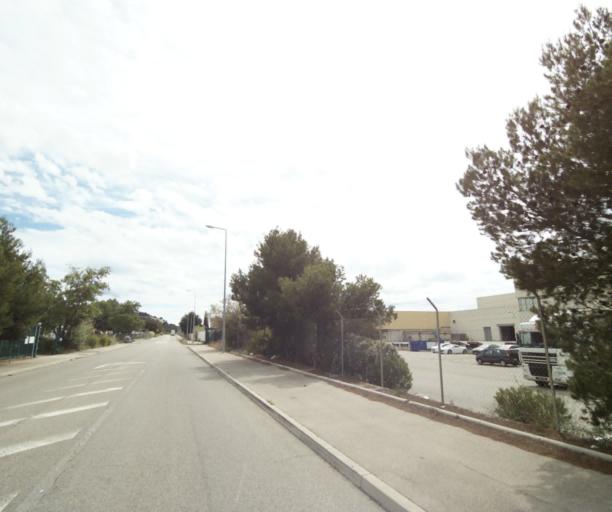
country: FR
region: Provence-Alpes-Cote d'Azur
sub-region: Departement des Bouches-du-Rhone
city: Rognac
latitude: 43.4774
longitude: 5.2339
